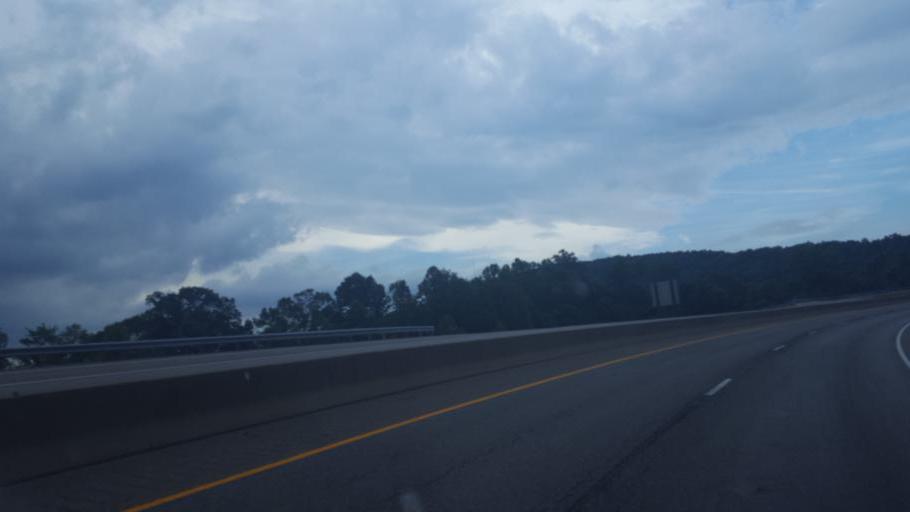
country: US
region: Kentucky
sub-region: Letcher County
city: Jenkins
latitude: 37.1584
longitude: -82.6398
